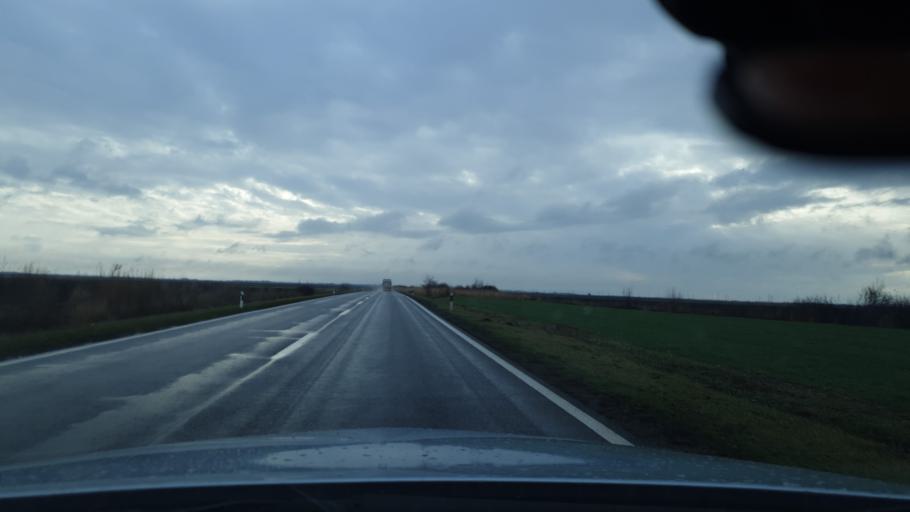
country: RS
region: Autonomna Pokrajina Vojvodina
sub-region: Juznobanatski Okrug
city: Kovin
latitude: 44.7949
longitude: 20.9109
